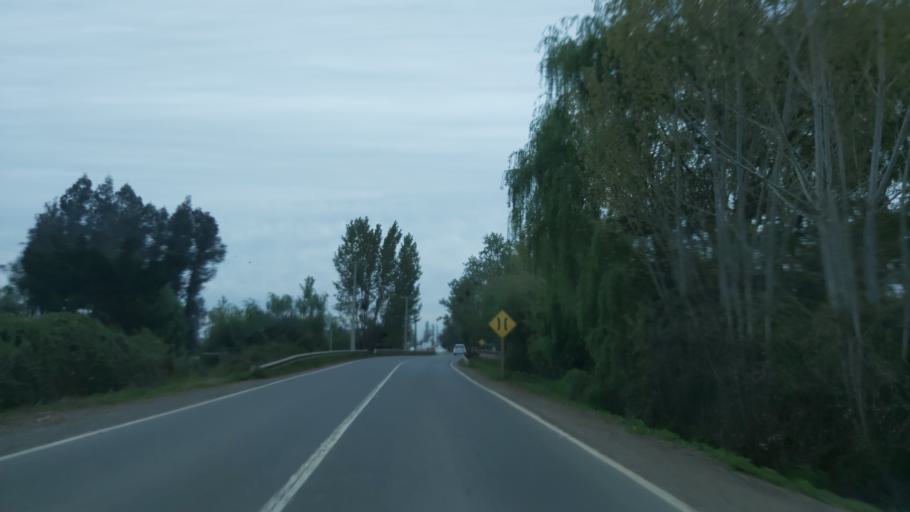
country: CL
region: Maule
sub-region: Provincia de Linares
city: Colbun
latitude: -35.7506
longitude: -71.4945
